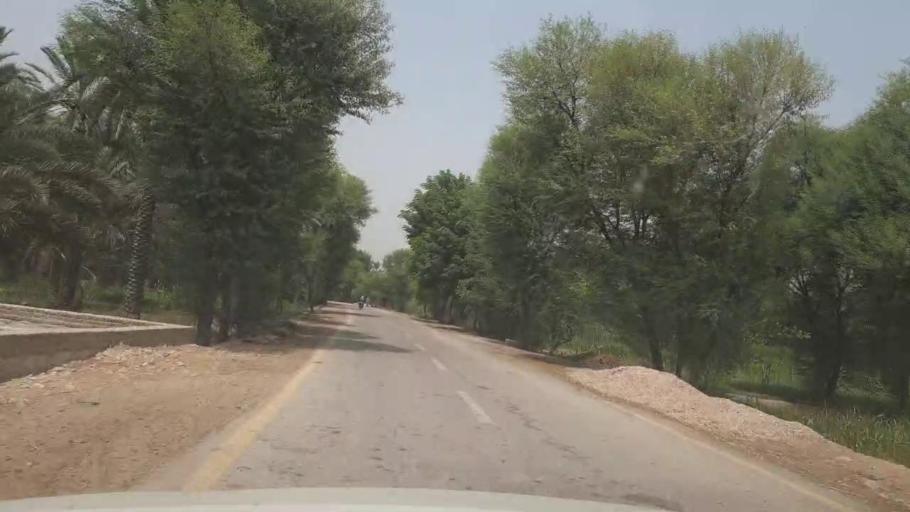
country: PK
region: Sindh
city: Kot Diji
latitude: 27.3660
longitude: 68.6466
